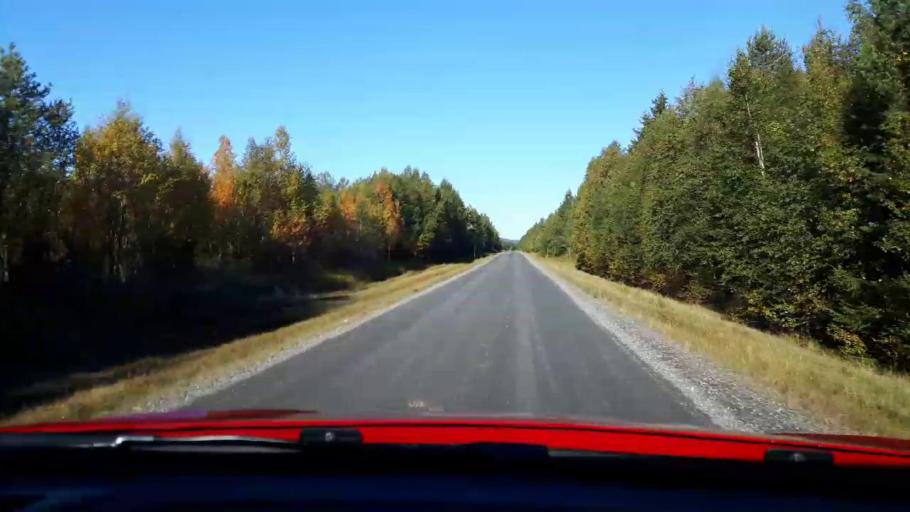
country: NO
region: Nord-Trondelag
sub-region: Lierne
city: Sandvika
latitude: 64.5256
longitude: 14.0623
